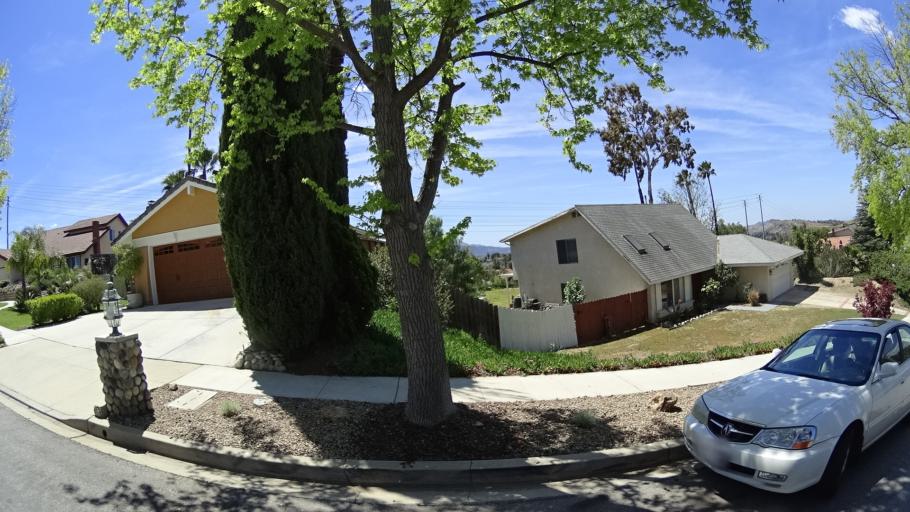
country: US
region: California
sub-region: Ventura County
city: Thousand Oaks
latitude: 34.2298
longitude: -118.8542
